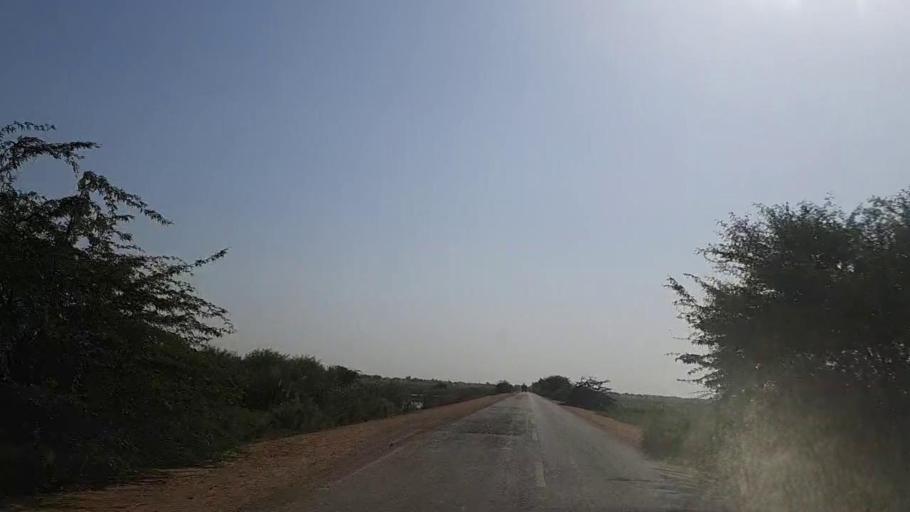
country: PK
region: Sindh
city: Mirpur Batoro
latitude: 24.5845
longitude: 68.2903
